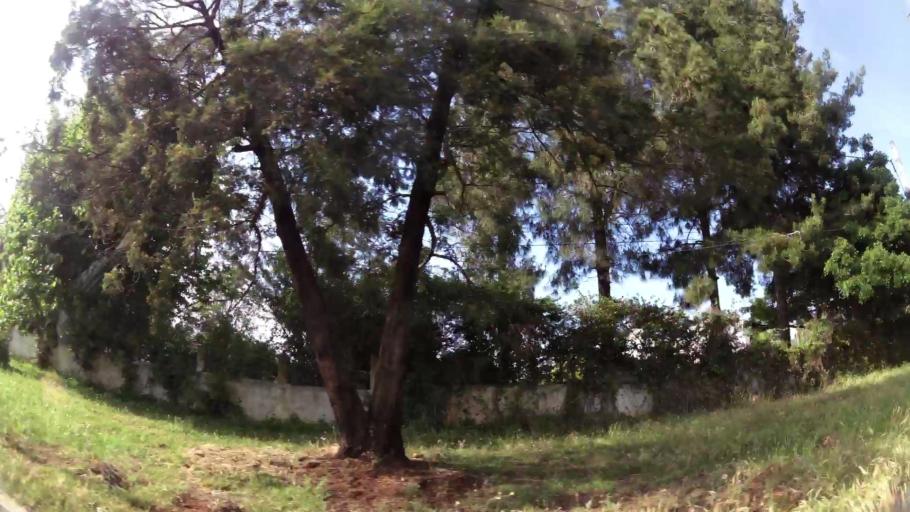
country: MA
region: Rabat-Sale-Zemmour-Zaer
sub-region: Rabat
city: Rabat
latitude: 33.9333
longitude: -6.8093
